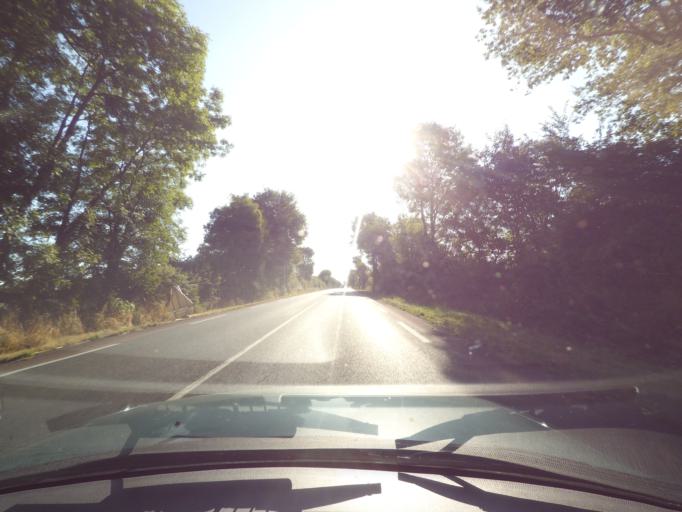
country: FR
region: Poitou-Charentes
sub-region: Departement des Deux-Sevres
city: La Peyratte
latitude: 46.6489
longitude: -0.1832
